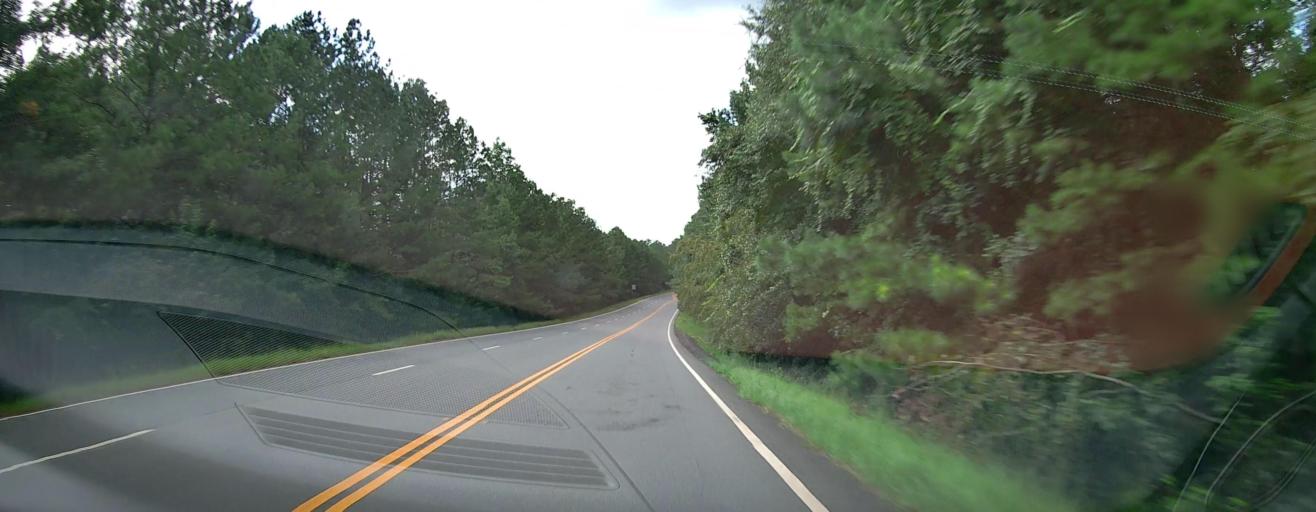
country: US
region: Georgia
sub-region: Bibb County
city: West Point
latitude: 32.8734
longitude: -83.9195
